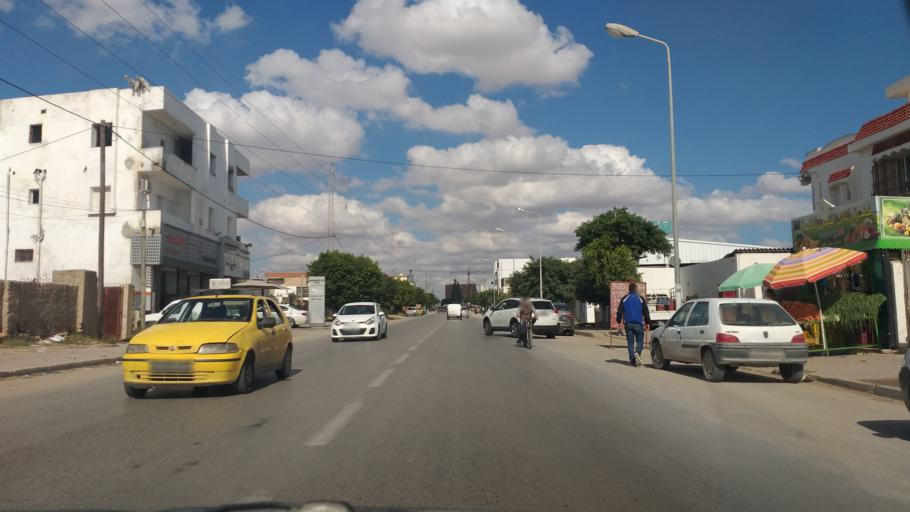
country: TN
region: Safaqis
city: Al Qarmadah
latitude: 34.7748
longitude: 10.7764
